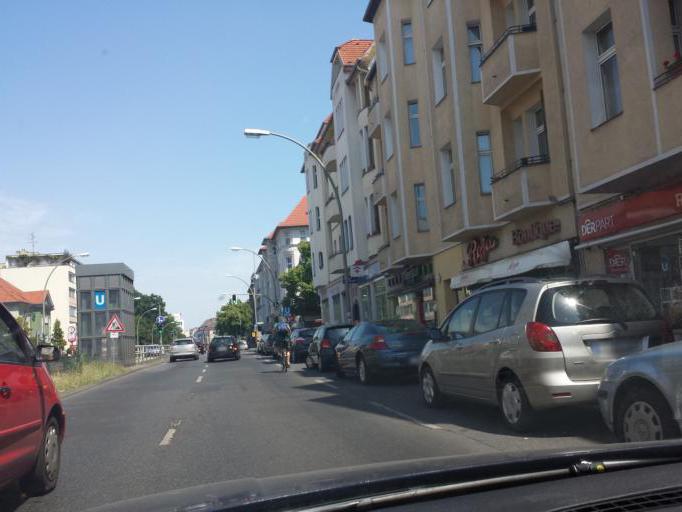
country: DE
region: Berlin
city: Tempelhof Bezirk
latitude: 52.4602
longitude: 13.3848
